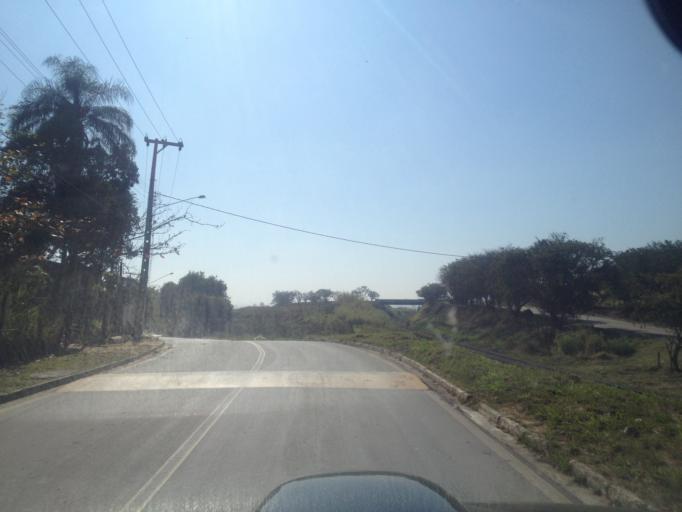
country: BR
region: Rio de Janeiro
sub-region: Porto Real
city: Porto Real
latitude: -22.4461
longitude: -44.3197
